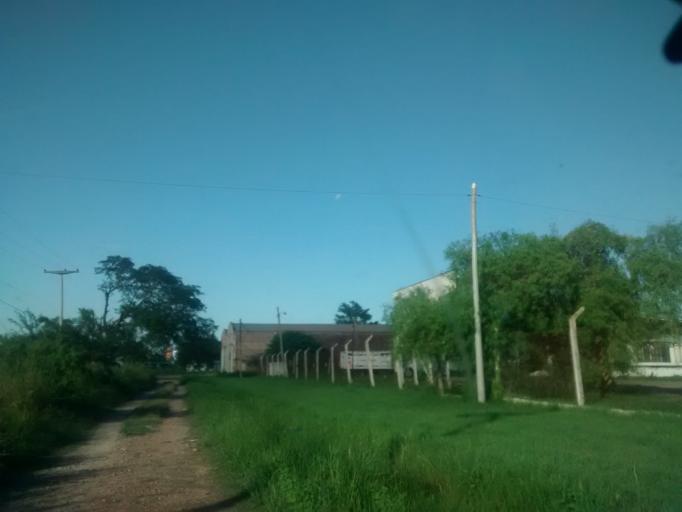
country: AR
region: Chaco
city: Fontana
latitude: -27.4539
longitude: -59.0313
